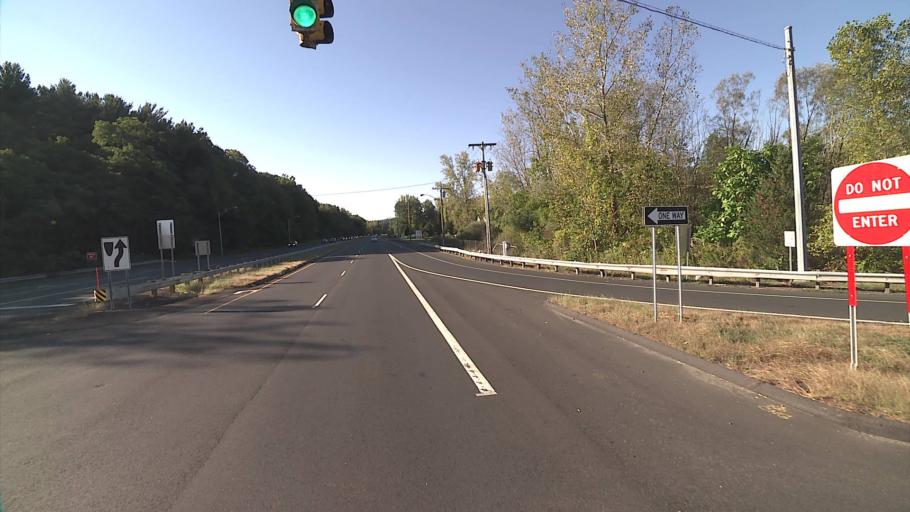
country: US
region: Connecticut
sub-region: Hartford County
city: Kensington
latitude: 41.6224
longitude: -72.7417
